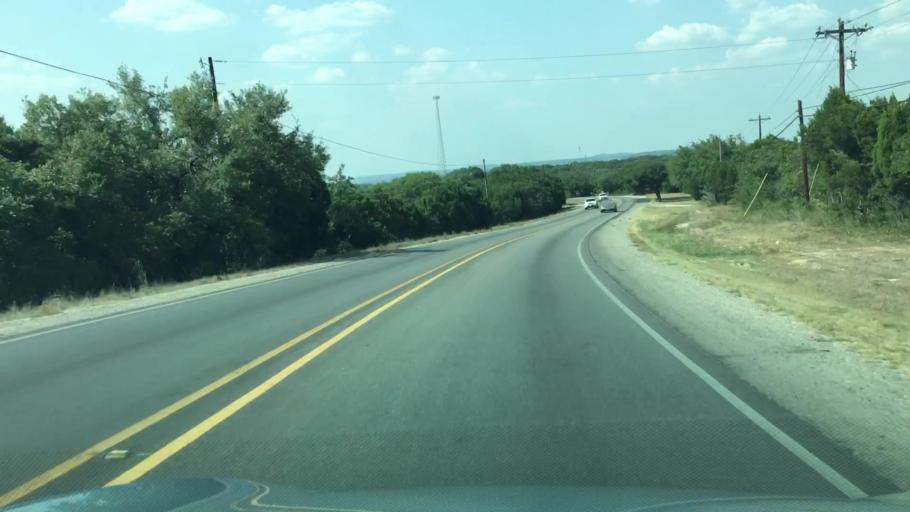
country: US
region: Texas
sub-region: Hays County
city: Wimberley
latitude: 29.9539
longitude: -98.0946
